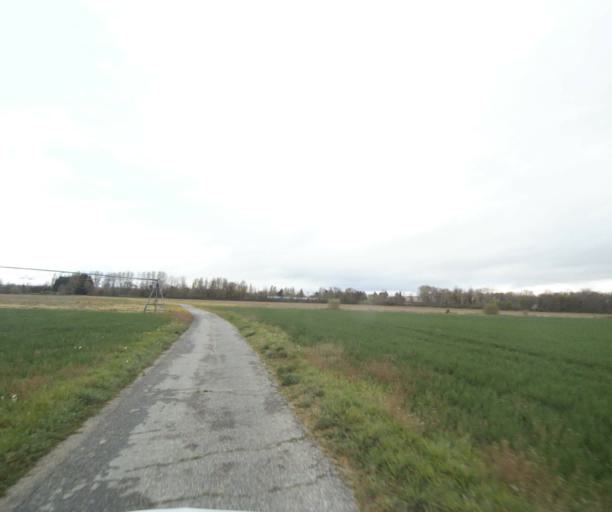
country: FR
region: Midi-Pyrenees
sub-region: Departement de l'Ariege
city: Saverdun
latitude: 43.2232
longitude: 1.5986
